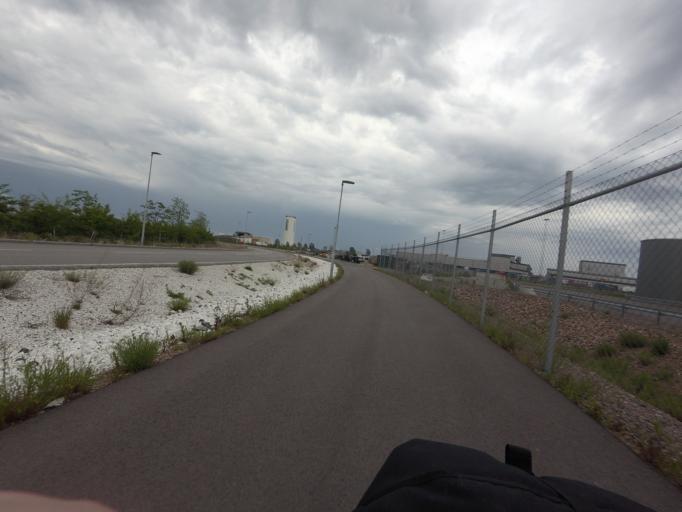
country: SE
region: Skane
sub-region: Malmo
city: Malmoe
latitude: 55.6316
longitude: 13.0068
